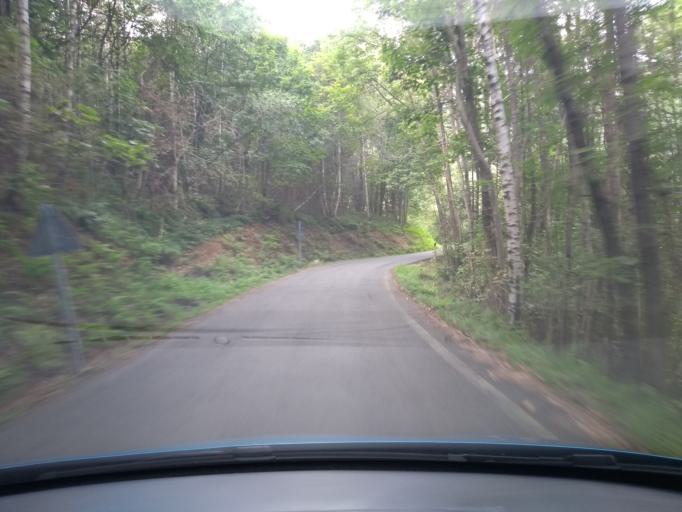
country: IT
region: Piedmont
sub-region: Provincia di Torino
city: Corio
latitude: 45.3313
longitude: 7.5152
